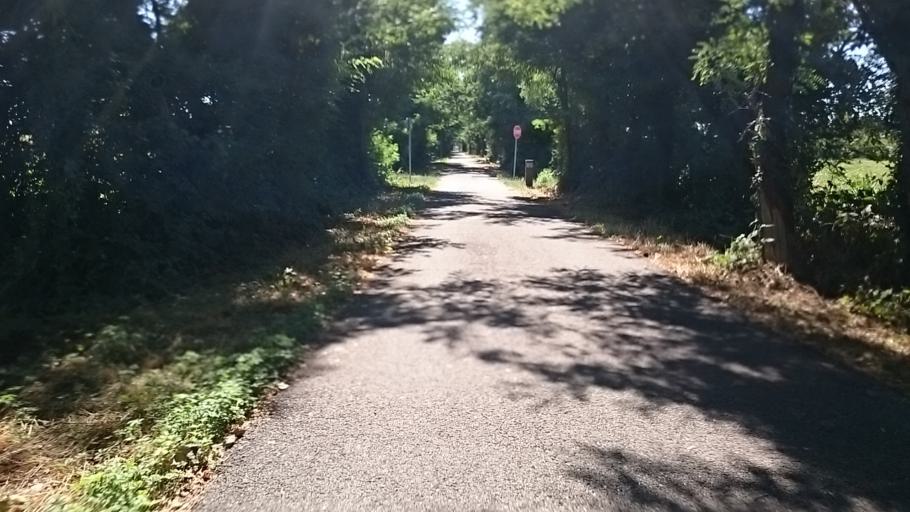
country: IT
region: Veneto
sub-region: Provincia di Padova
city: Piombino Dese
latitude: 45.5933
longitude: 11.9765
